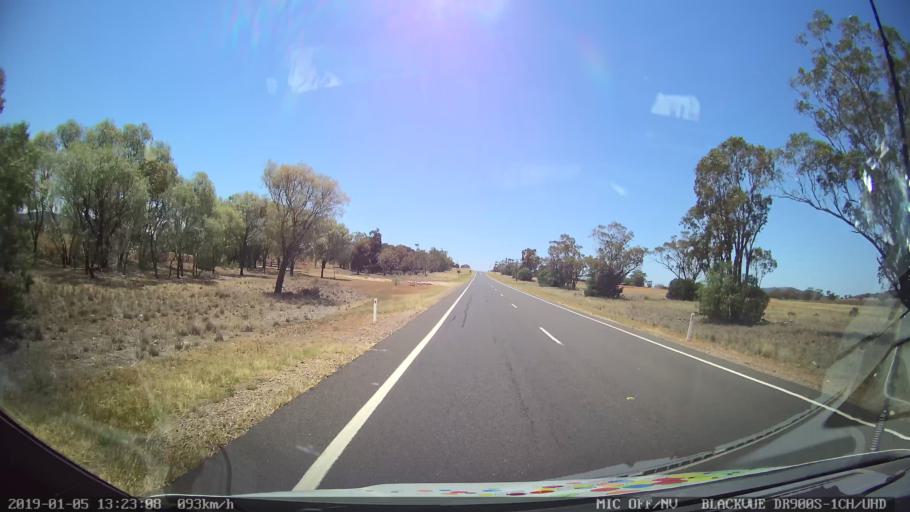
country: AU
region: New South Wales
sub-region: Gunnedah
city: Gunnedah
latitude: -31.0804
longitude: 149.9713
